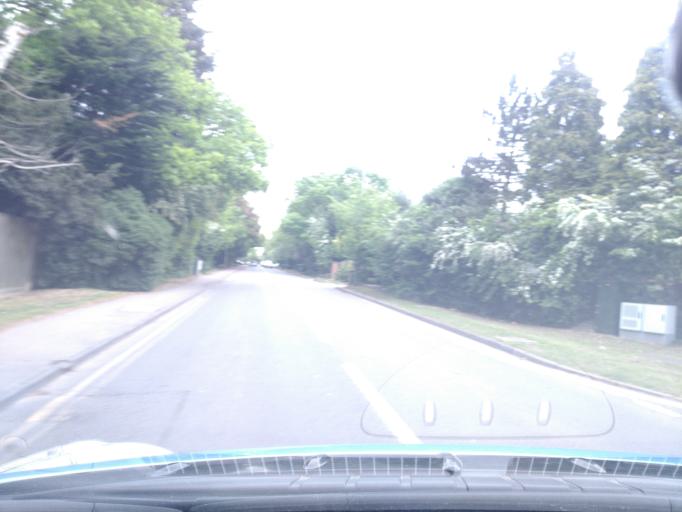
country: GB
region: England
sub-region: Greater London
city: High Barnet
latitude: 51.6426
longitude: -0.2417
